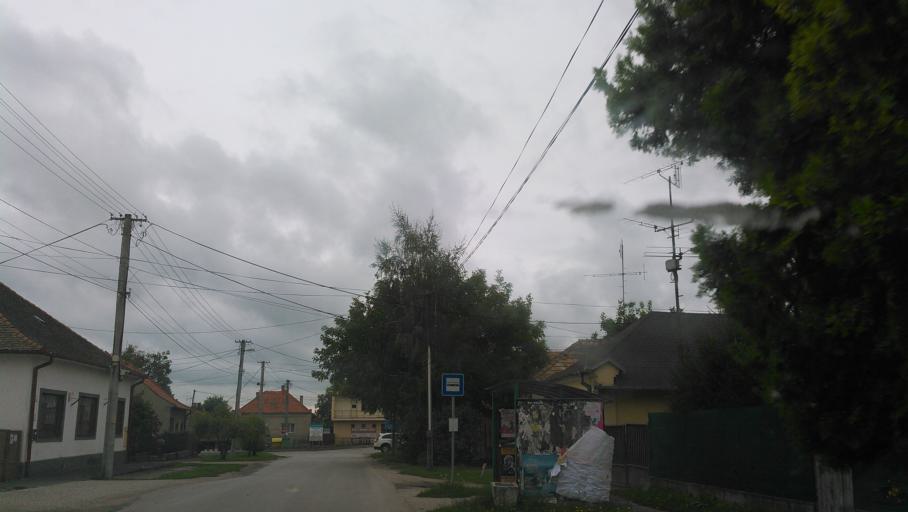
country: SK
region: Trnavsky
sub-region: Okres Dunajska Streda
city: Velky Meder
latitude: 47.8858
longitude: 17.8090
